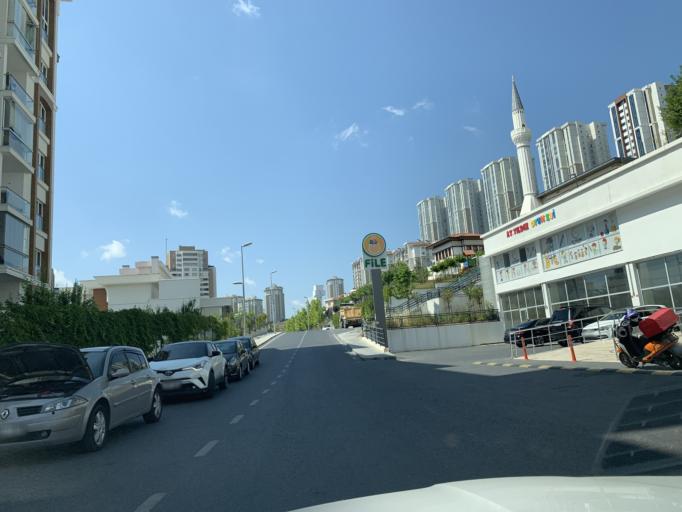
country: TR
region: Istanbul
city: Esenyurt
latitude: 41.0755
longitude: 28.6949
